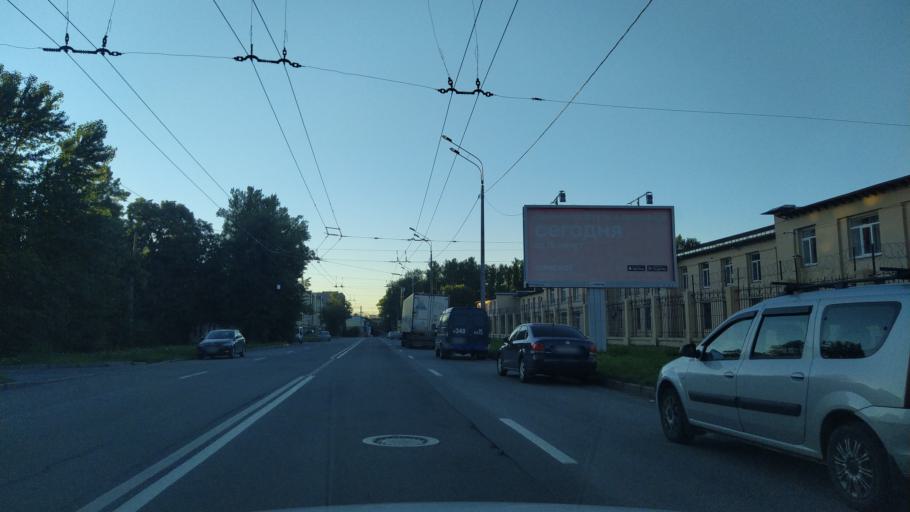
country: RU
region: Leningrad
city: Finlyandskiy
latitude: 59.9688
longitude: 30.3658
